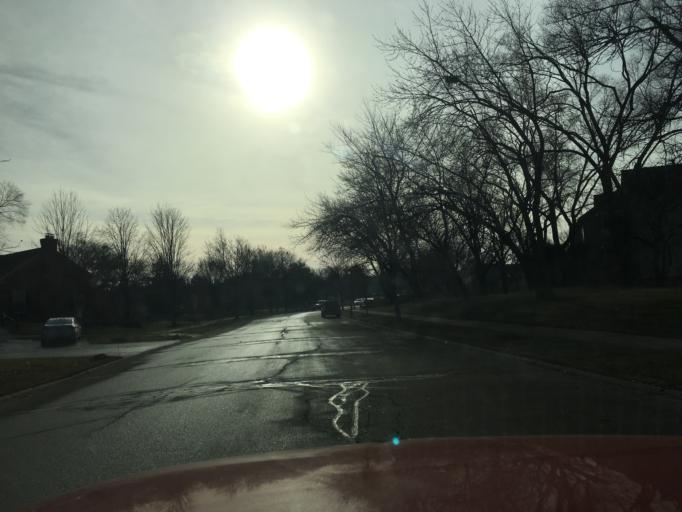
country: US
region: Illinois
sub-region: Cook County
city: Buffalo Grove
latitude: 42.1436
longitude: -87.9570
